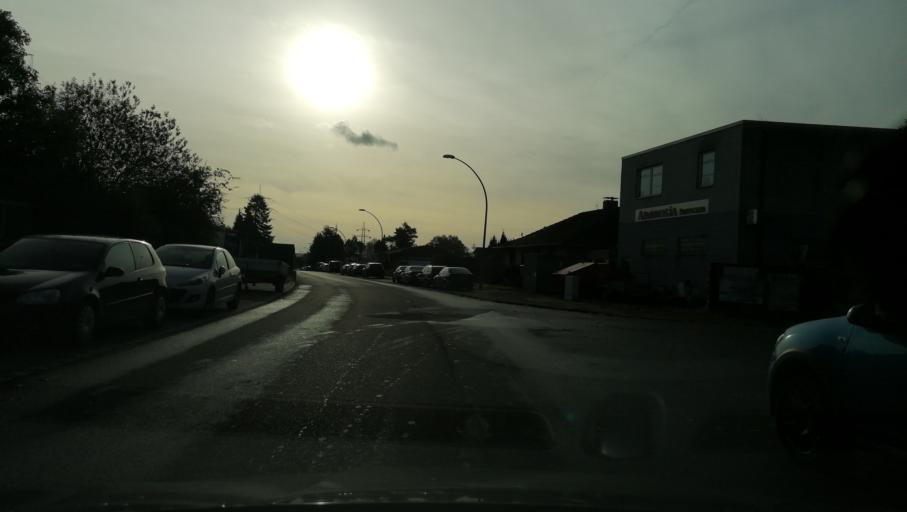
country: DE
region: North Rhine-Westphalia
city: Herten
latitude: 51.6032
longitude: 7.1024
